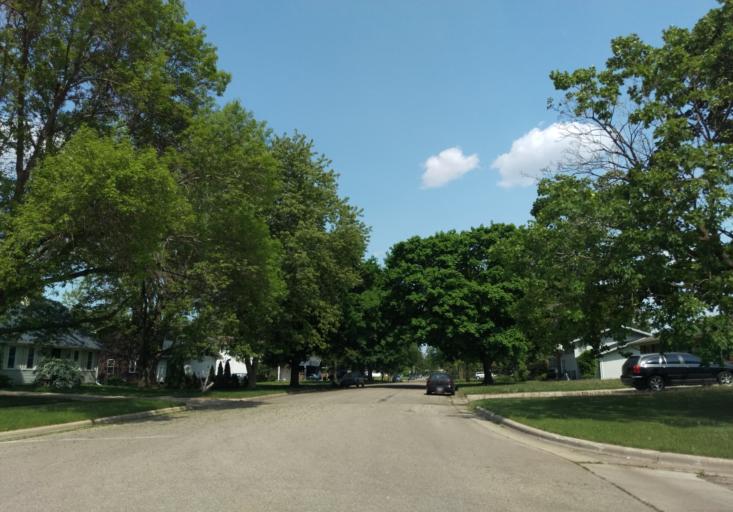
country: US
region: Wisconsin
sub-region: Rock County
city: Evansville
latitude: 42.7752
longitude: -89.3119
